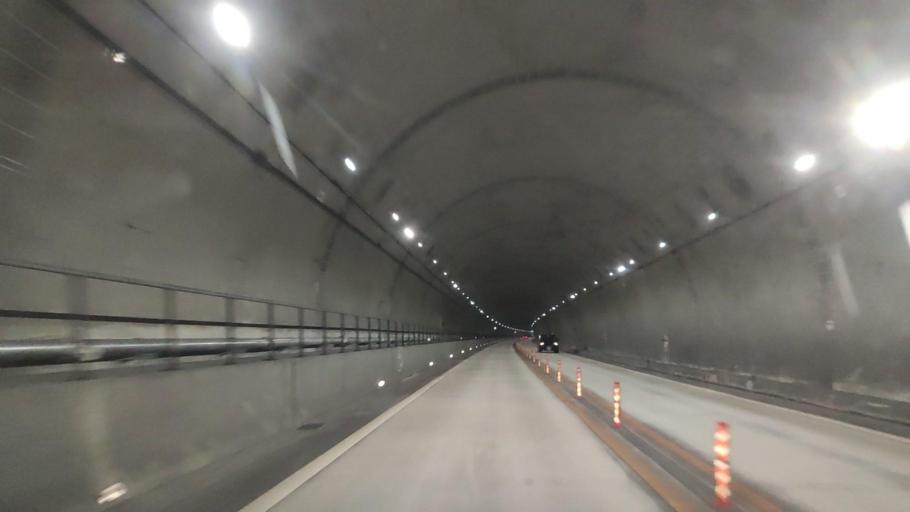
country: JP
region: Ehime
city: Hojo
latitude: 34.0788
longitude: 132.9762
